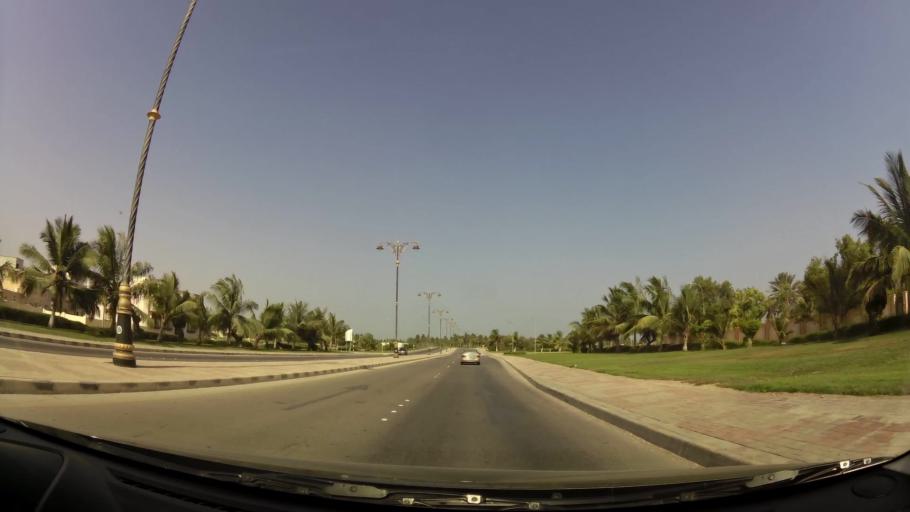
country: OM
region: Zufar
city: Salalah
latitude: 17.0028
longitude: 54.0646
